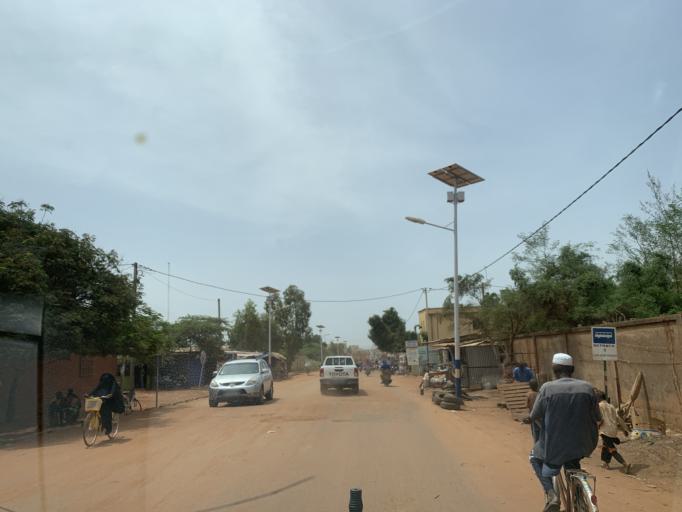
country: BF
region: Centre
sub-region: Kadiogo Province
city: Ouagadougou
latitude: 12.3339
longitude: -1.4956
